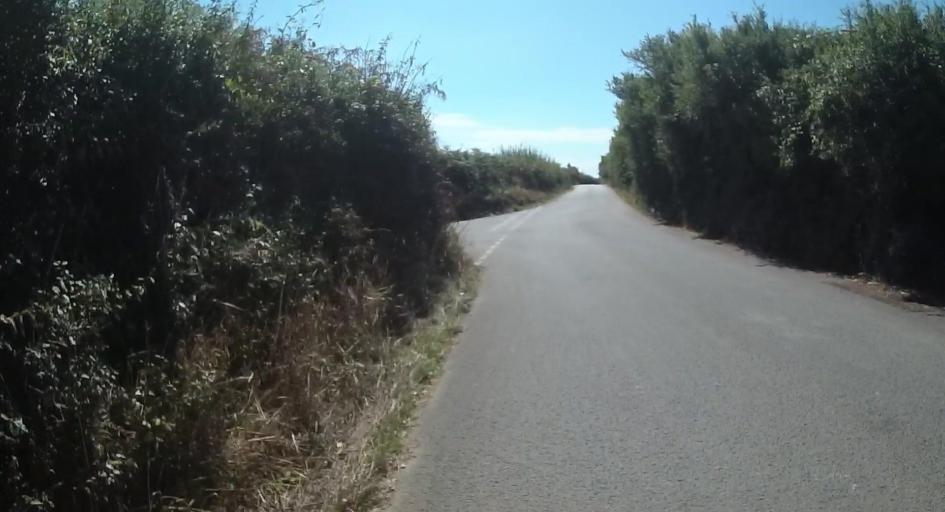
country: GB
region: England
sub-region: Isle of Wight
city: Chale
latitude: 50.6105
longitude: -1.3240
